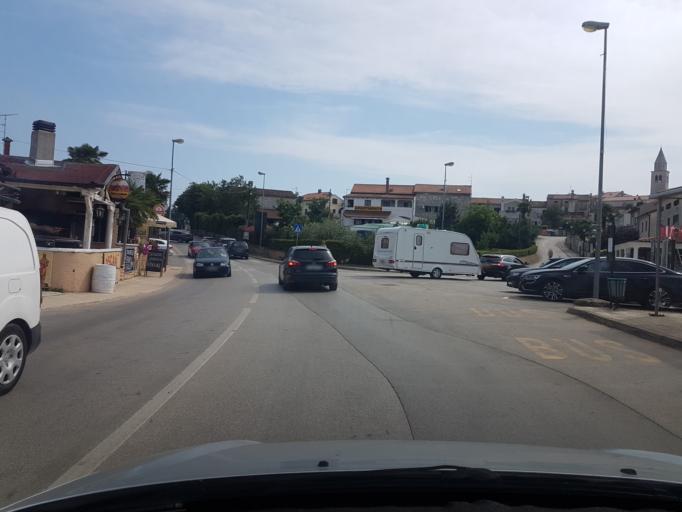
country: HR
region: Istarska
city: Vrsar
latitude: 45.1746
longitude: 13.6063
